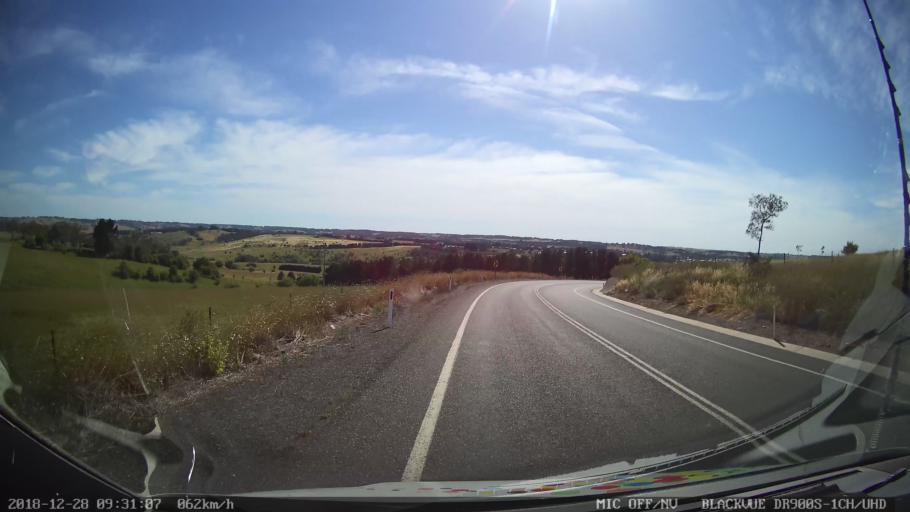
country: AU
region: New South Wales
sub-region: Upper Lachlan Shire
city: Crookwell
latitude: -34.4489
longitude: 149.4430
